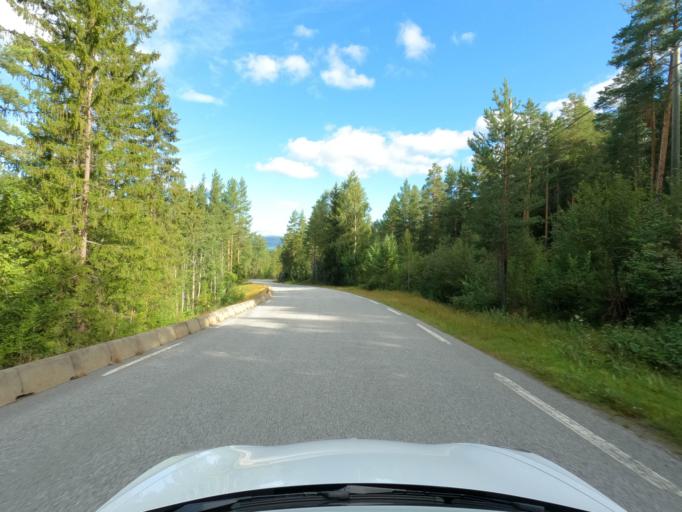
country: NO
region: Telemark
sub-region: Tinn
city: Rjukan
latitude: 59.9824
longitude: 8.8555
